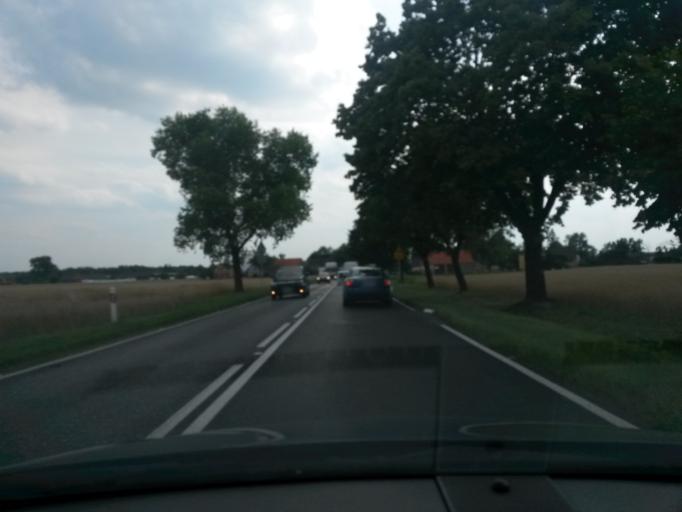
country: PL
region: Greater Poland Voivodeship
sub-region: Powiat poznanski
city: Kornik
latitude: 52.1858
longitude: 17.0558
